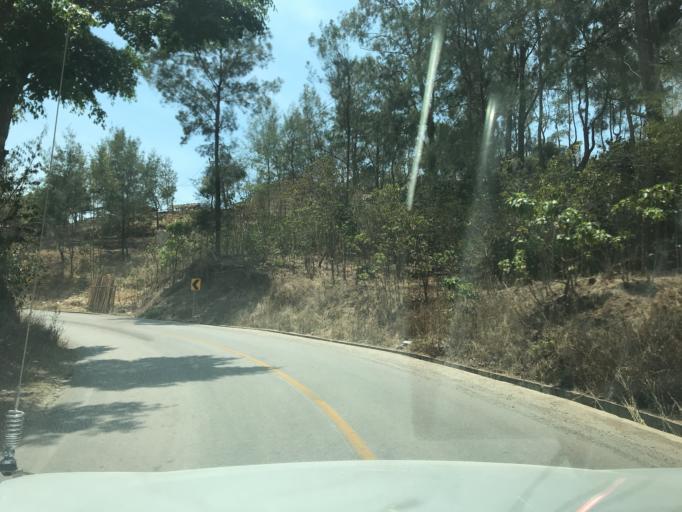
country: TL
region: Aileu
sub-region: Aileu Villa
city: Aileu
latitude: -8.8062
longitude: 125.5937
